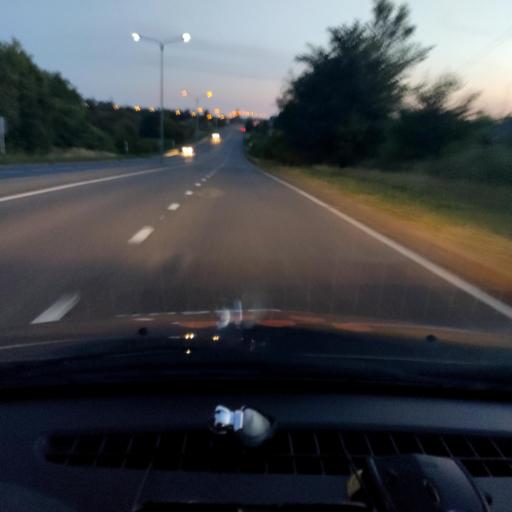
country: RU
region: Belgorod
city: Gubkin
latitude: 51.2757
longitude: 37.5899
